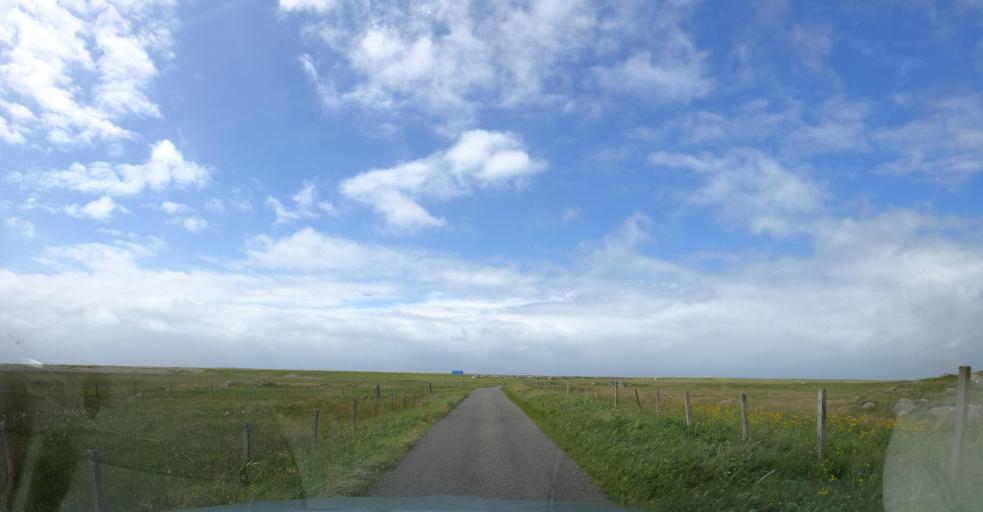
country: GB
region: Scotland
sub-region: Eilean Siar
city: Isle of South Uist
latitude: 57.2799
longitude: -7.4165
